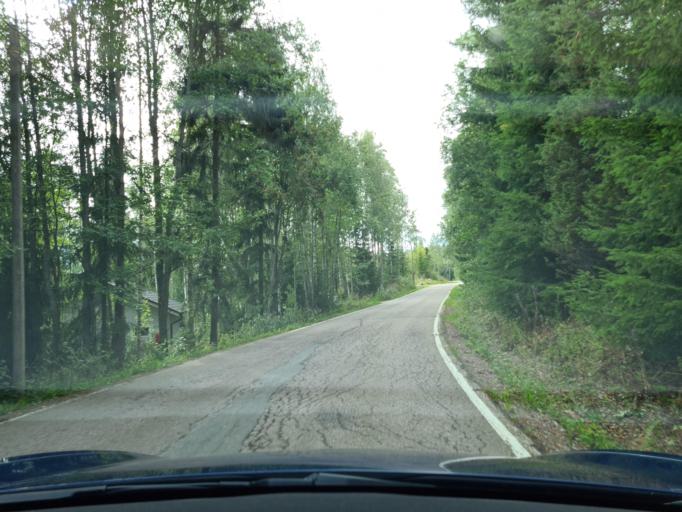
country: FI
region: Uusimaa
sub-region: Helsinki
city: Vihti
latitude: 60.4589
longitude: 24.4210
